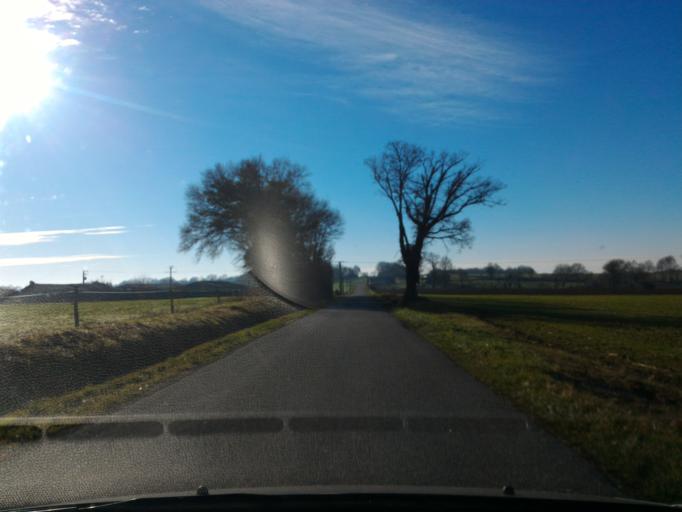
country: FR
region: Poitou-Charentes
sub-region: Departement de la Charente
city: Champagne-Mouton
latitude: 45.9835
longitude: 0.4018
